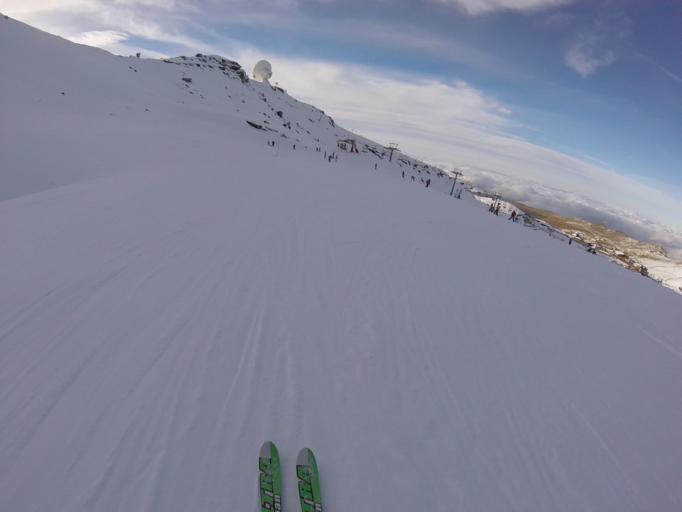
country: ES
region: Andalusia
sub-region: Provincia de Granada
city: Capileira
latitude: 37.0646
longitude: -3.3867
